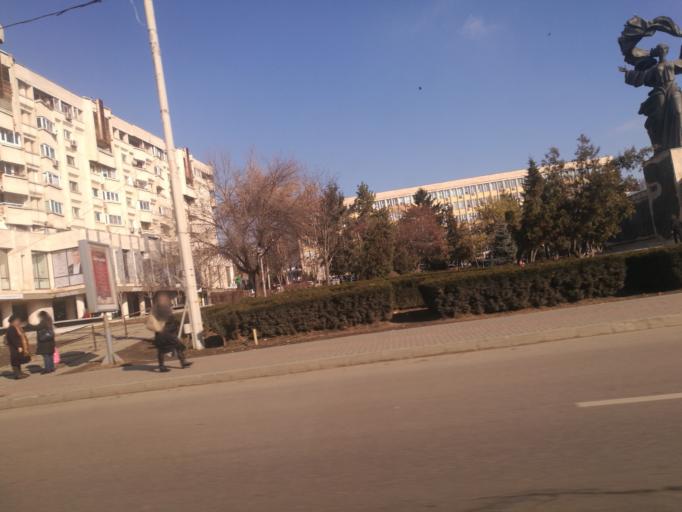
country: RO
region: Iasi
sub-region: Municipiul Iasi
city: Iasi
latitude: 47.1682
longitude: 27.5802
